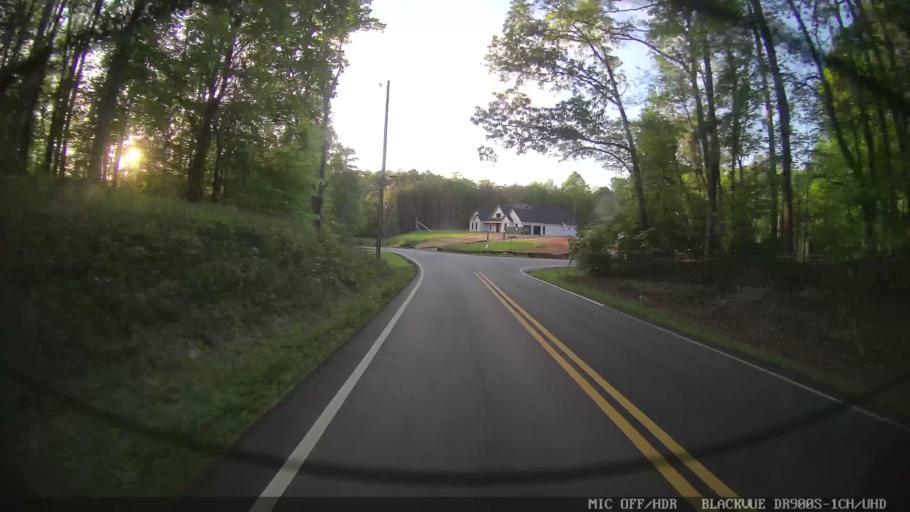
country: US
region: Georgia
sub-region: Bartow County
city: Emerson
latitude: 34.0913
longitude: -84.7656
